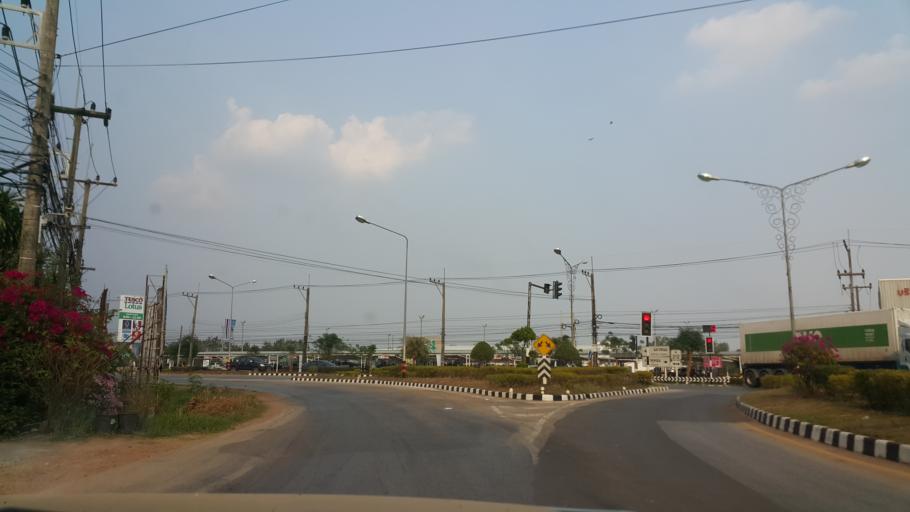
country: TH
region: Nakhon Phanom
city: That Phanom
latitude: 16.9567
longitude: 104.7250
